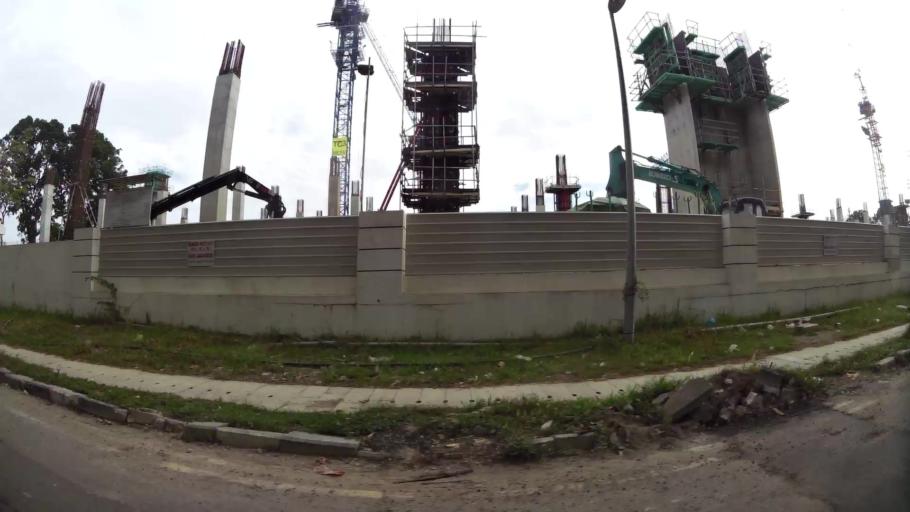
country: MY
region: Johor
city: Johor Bahru
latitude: 1.3176
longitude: 103.6529
